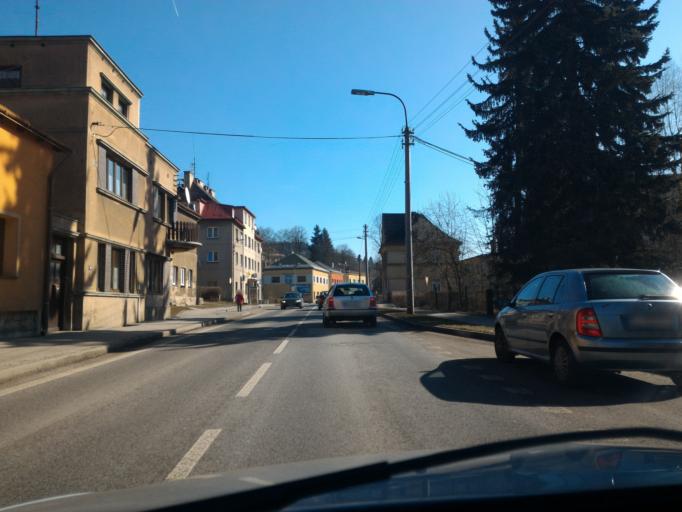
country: CZ
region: Liberecky
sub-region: Okres Jablonec nad Nisou
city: Lucany nad Nisou
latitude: 50.7411
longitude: 15.2184
